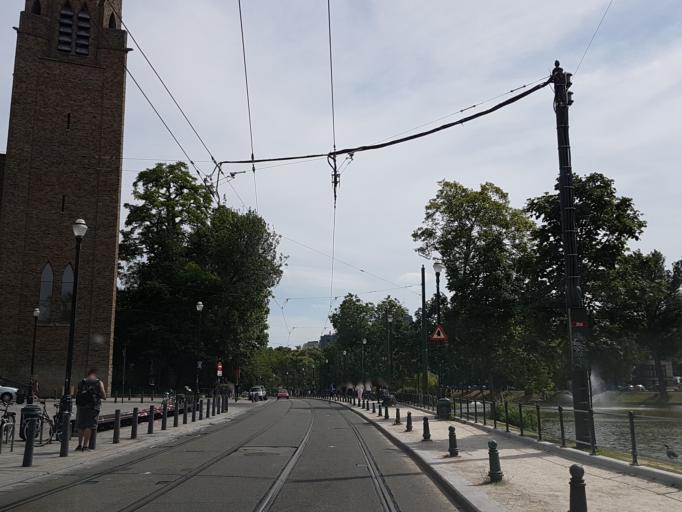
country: BE
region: Brussels Capital
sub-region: Bruxelles-Capitale
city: Brussels
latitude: 50.8269
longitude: 4.3723
